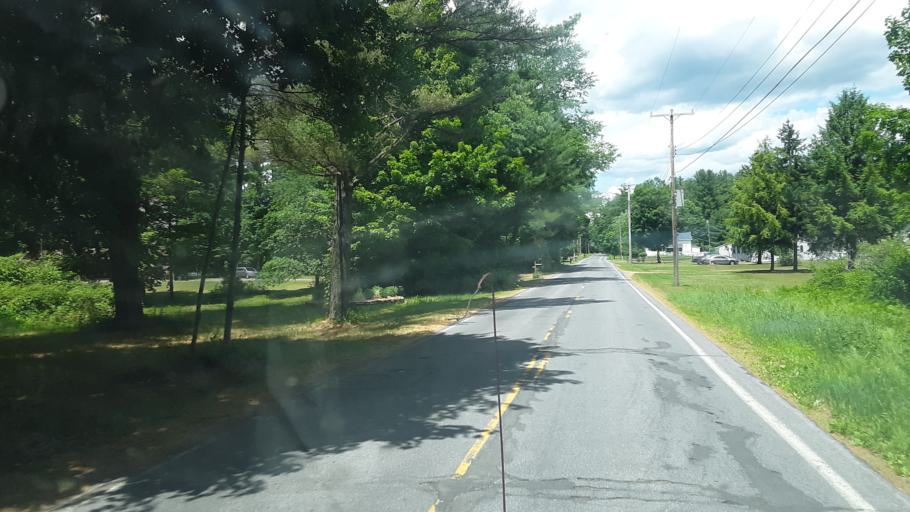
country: US
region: New York
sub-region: Oneida County
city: Rome
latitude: 43.2437
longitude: -75.5973
